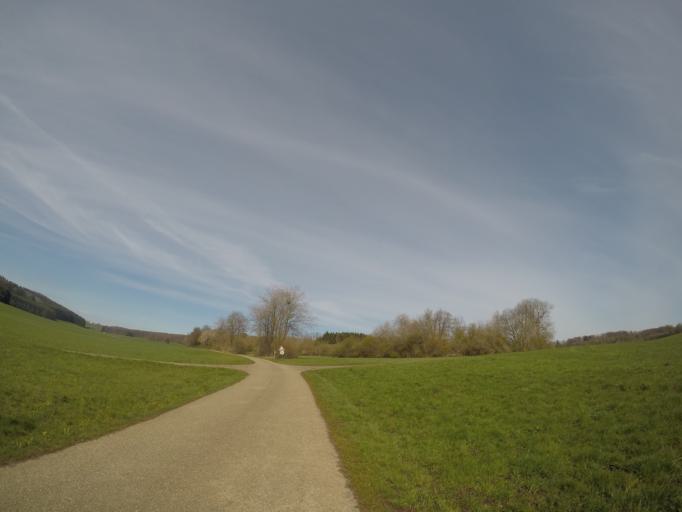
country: DE
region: Baden-Wuerttemberg
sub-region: Regierungsbezirk Stuttgart
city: Hohenstadt
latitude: 48.5274
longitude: 9.6660
